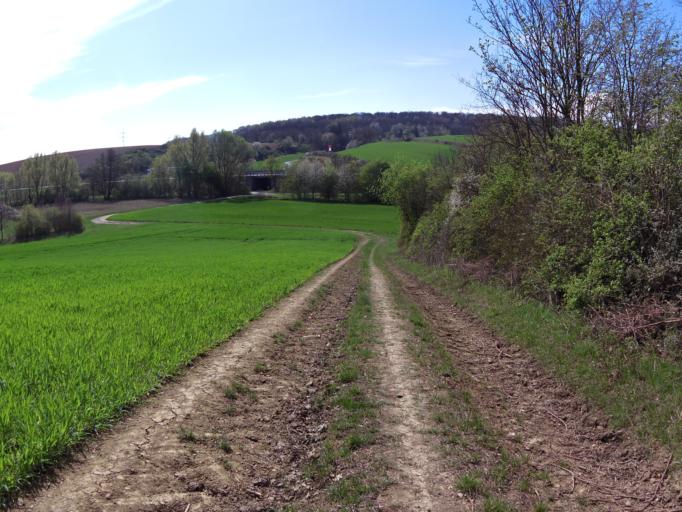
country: DE
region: Bavaria
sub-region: Regierungsbezirk Unterfranken
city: Rottendorf
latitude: 49.7845
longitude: 10.0404
